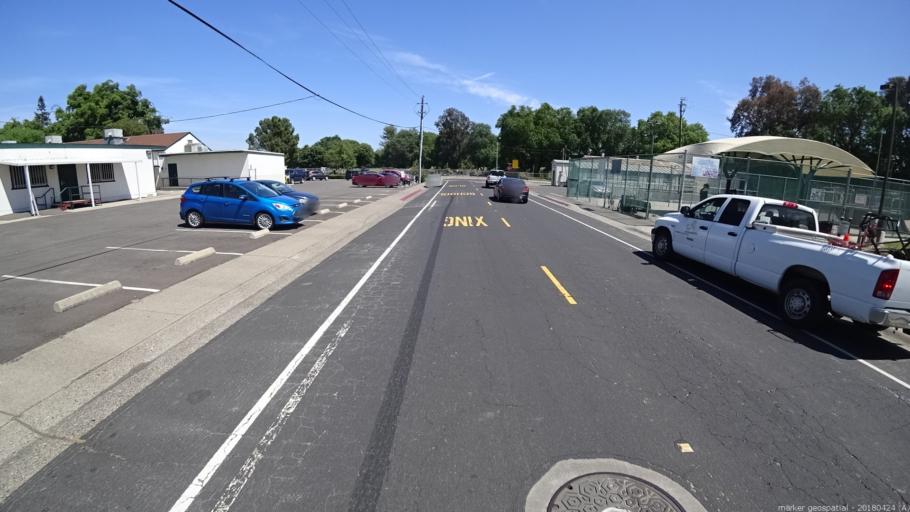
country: US
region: California
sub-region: Yolo County
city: West Sacramento
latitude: 38.5769
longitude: -121.5315
